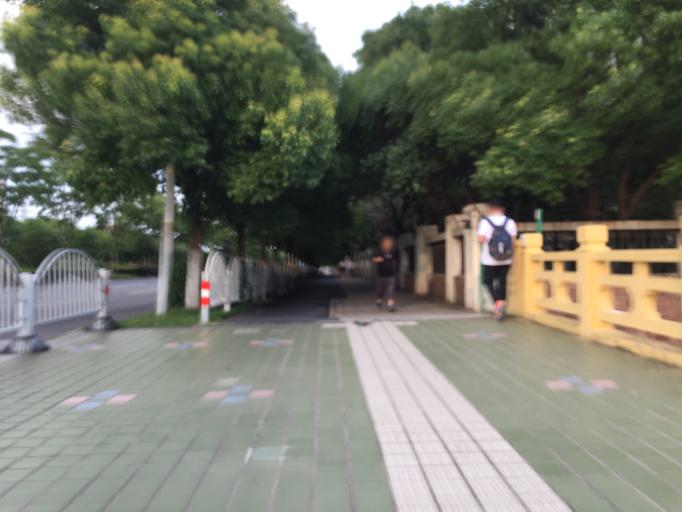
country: CN
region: Shanghai Shi
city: Huamu
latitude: 31.1896
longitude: 121.5372
